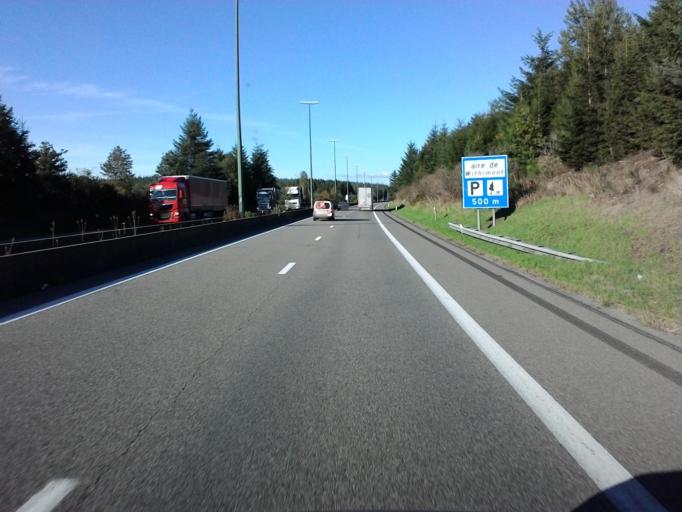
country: BE
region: Wallonia
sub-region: Province du Luxembourg
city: Bastogne
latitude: 50.0343
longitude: 5.7026
